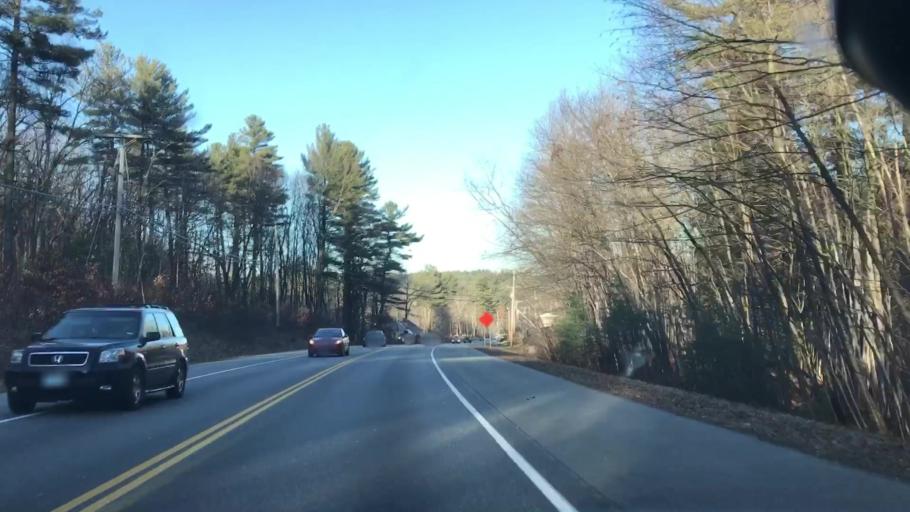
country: US
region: New Hampshire
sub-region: Hillsborough County
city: Bedford
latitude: 42.9326
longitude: -71.5312
